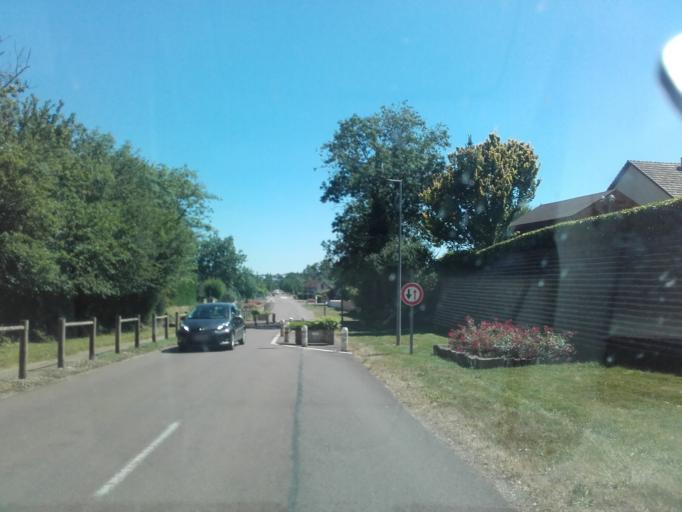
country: FR
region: Bourgogne
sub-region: Departement de la Cote-d'Or
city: Corpeau
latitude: 46.9269
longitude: 4.7525
